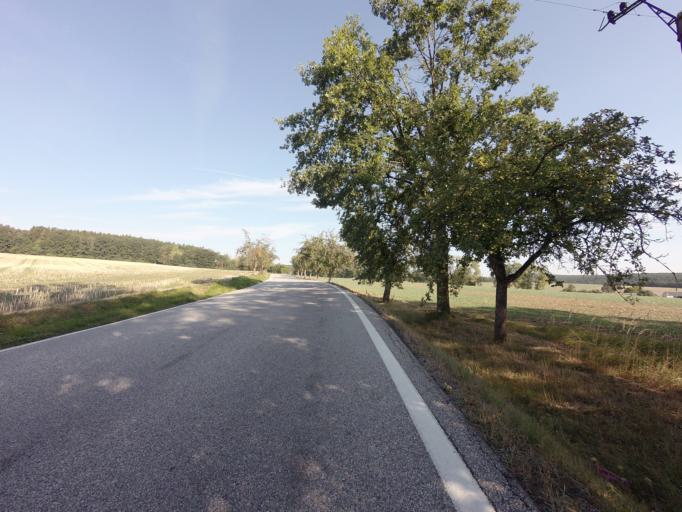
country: CZ
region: Jihocesky
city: Tyn nad Vltavou
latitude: 49.2569
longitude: 14.4170
